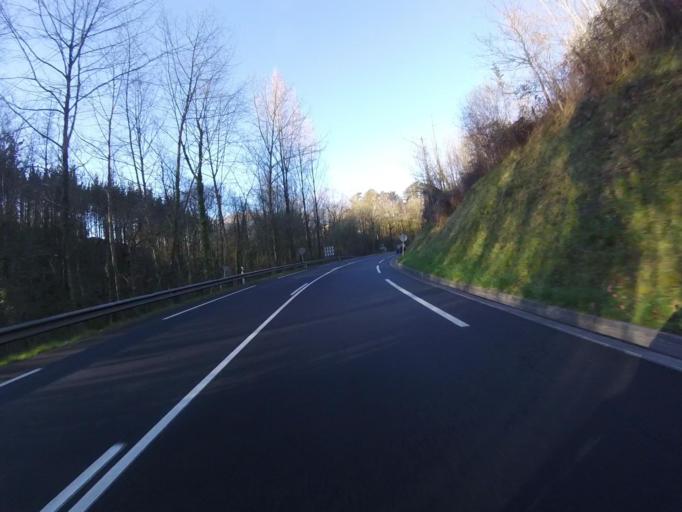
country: ES
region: Basque Country
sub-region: Provincia de Guipuzcoa
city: Errenteria
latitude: 43.2835
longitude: -1.9033
